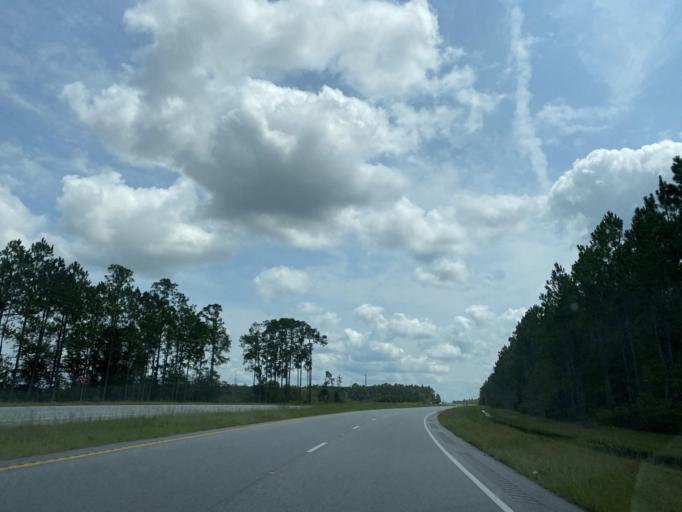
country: US
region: Georgia
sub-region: Ware County
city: Deenwood
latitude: 31.2678
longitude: -82.4329
